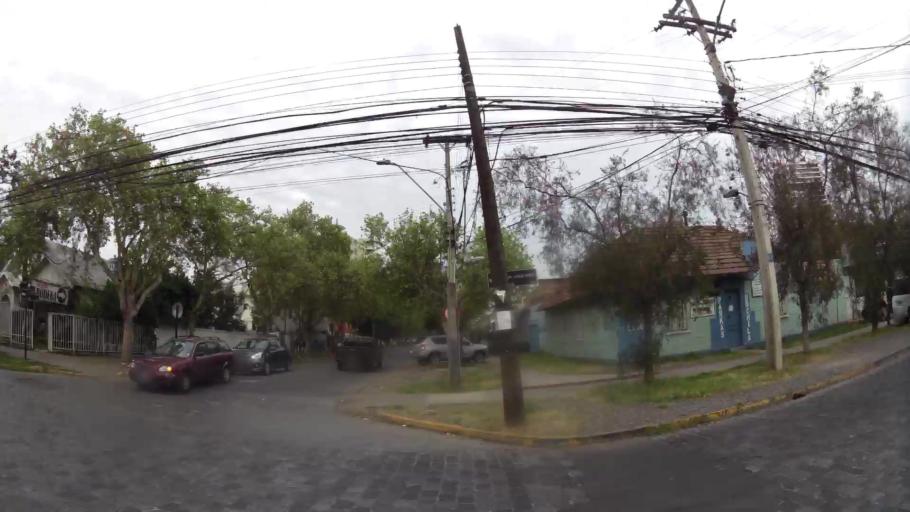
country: CL
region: Santiago Metropolitan
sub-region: Provincia de Santiago
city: Villa Presidente Frei, Nunoa, Santiago, Chile
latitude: -33.4524
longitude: -70.6125
